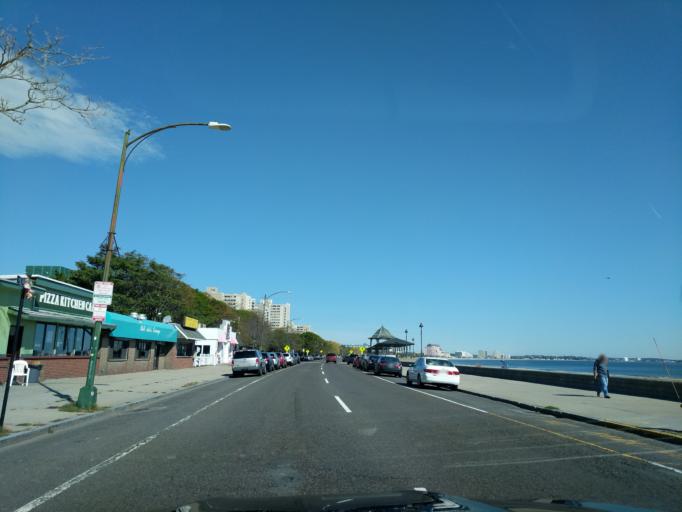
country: US
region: Massachusetts
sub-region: Suffolk County
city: Revere
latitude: 42.4063
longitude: -70.9915
